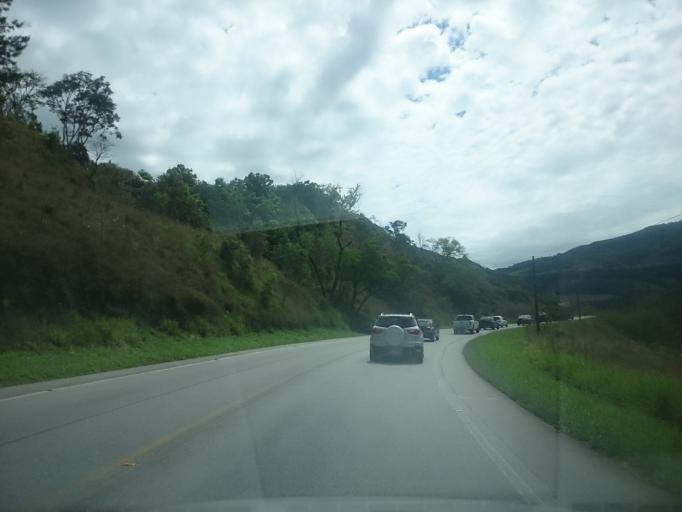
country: BR
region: Santa Catarina
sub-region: Anitapolis
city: Anitapolis
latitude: -27.6991
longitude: -49.2987
